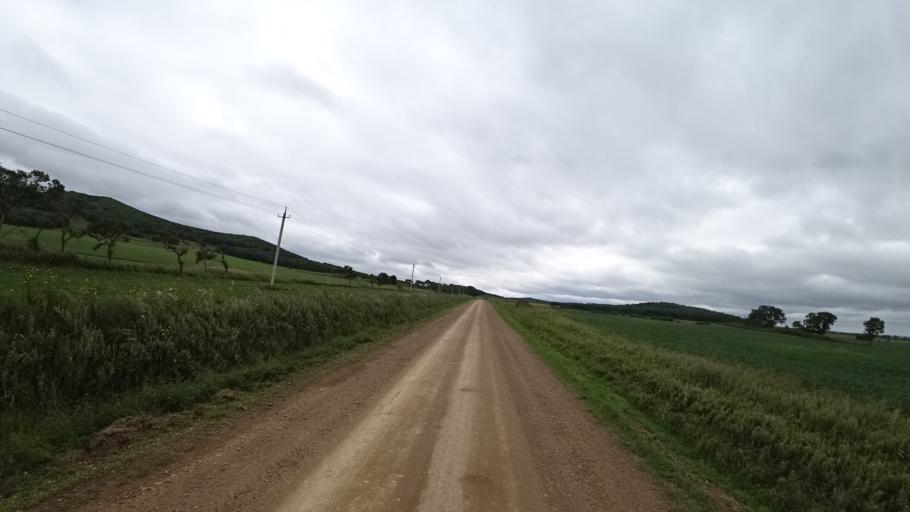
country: RU
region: Primorskiy
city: Chernigovka
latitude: 44.4755
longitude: 132.5798
